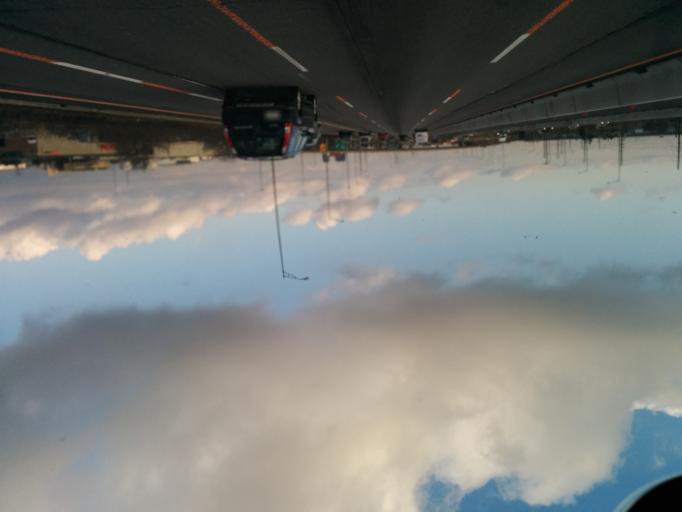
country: CA
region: Ontario
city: Etobicoke
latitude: 43.6920
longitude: -79.6041
